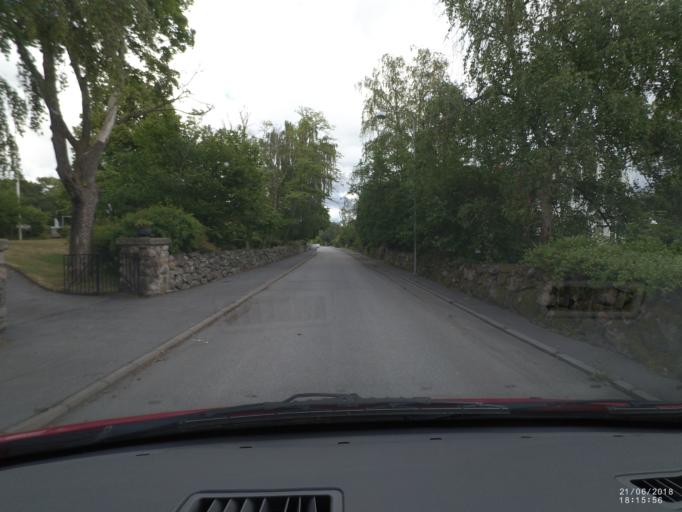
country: SE
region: Soedermanland
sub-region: Nykopings Kommun
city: Nykoping
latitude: 58.7569
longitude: 17.0230
